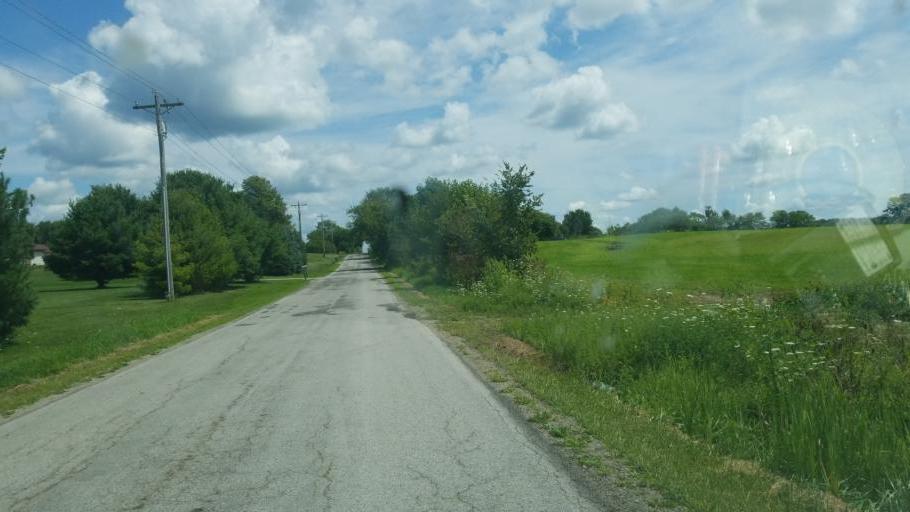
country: US
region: Ohio
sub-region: Knox County
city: Centerburg
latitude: 40.3643
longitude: -82.7328
